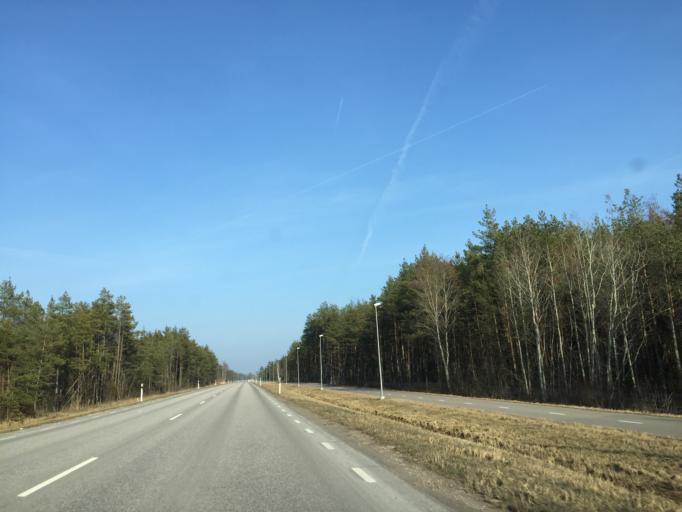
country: EE
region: Saare
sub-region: Kuressaare linn
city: Kuressaare
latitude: 58.2335
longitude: 22.4212
